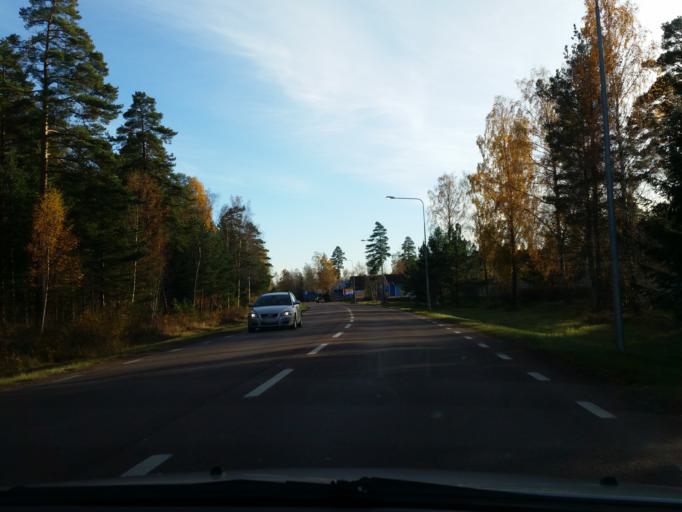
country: AX
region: Mariehamns stad
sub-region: Mariehamn
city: Mariehamn
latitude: 60.1213
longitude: 19.9342
